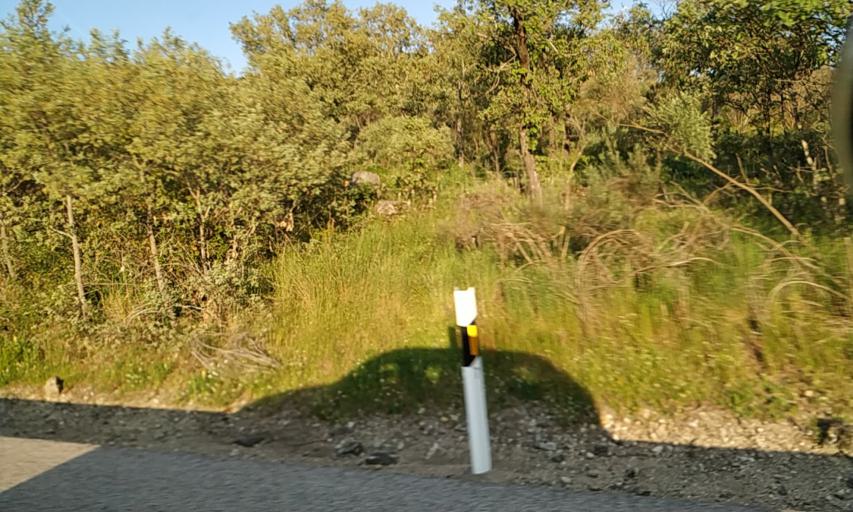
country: ES
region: Extremadura
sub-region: Provincia de Caceres
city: Valencia de Alcantara
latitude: 39.3792
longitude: -7.2516
